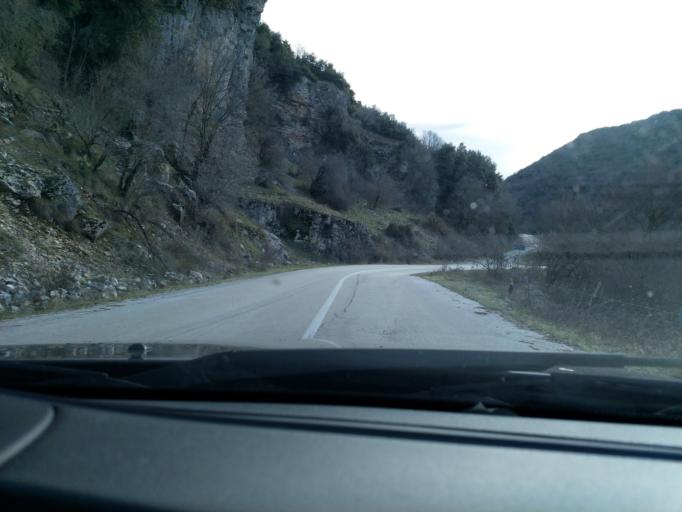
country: GR
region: Epirus
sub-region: Nomos Ioanninon
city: Asprangeloi
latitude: 39.8680
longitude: 20.7217
